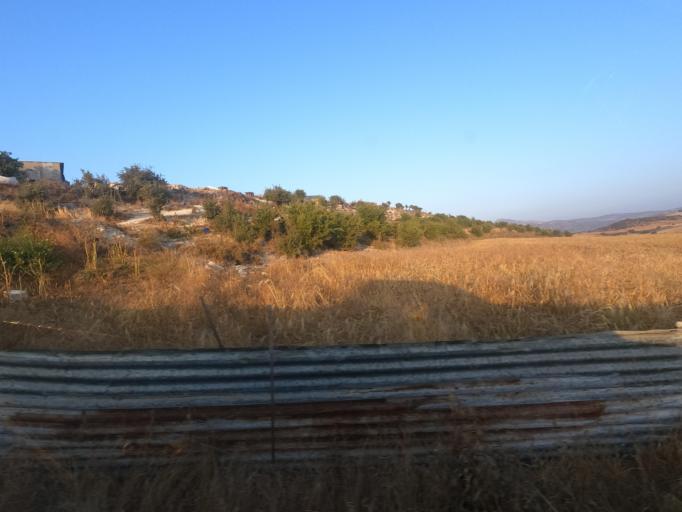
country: CY
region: Larnaka
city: Tersefanou
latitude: 34.8986
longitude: 33.5136
